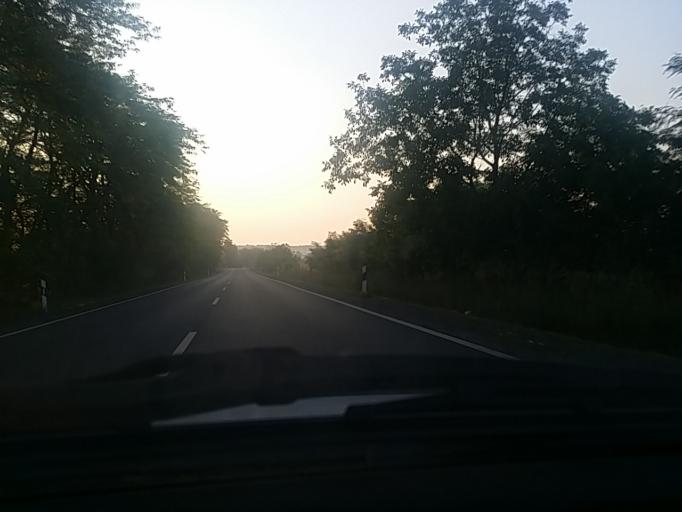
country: HU
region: Pest
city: Maglod
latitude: 47.4475
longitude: 19.3803
